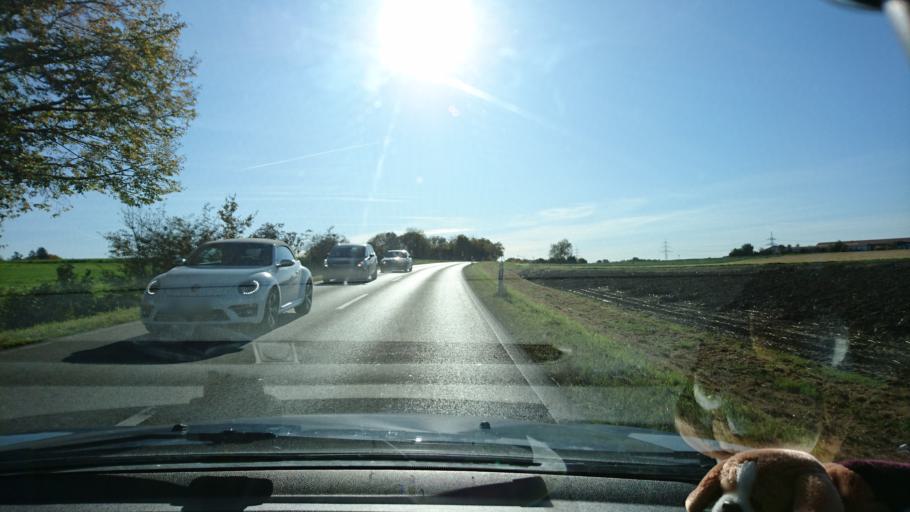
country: DE
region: Bavaria
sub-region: Upper Bavaria
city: Zorneding
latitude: 48.1004
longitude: 11.8295
